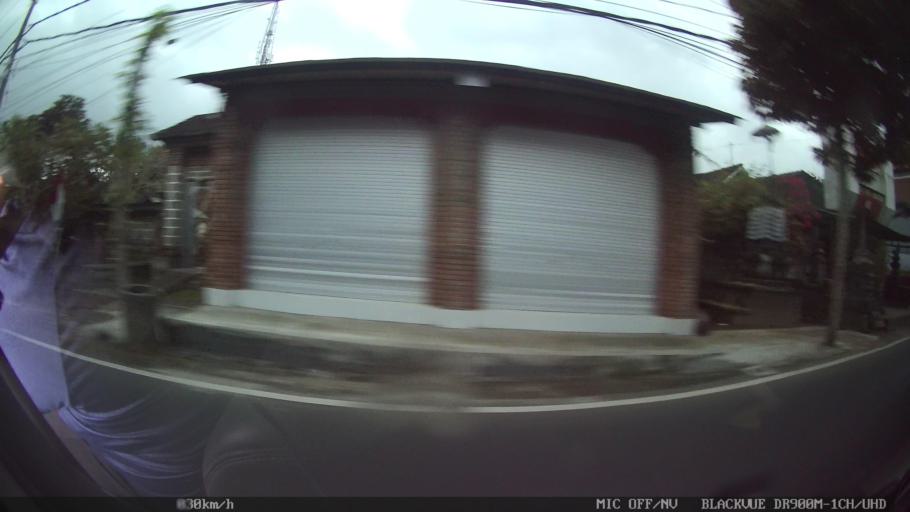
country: ID
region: Bali
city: Badung
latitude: -8.4366
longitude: 115.2447
